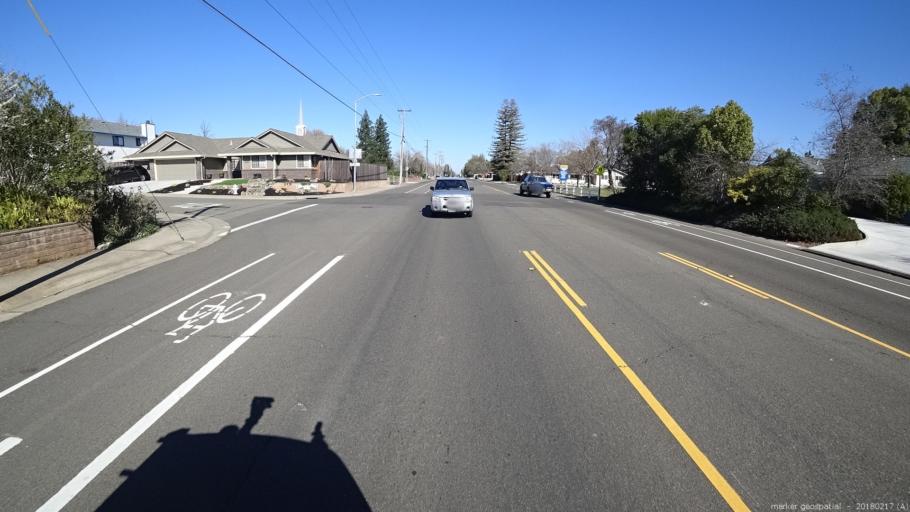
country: US
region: California
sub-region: Sacramento County
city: Orangevale
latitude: 38.6645
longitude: -121.2025
